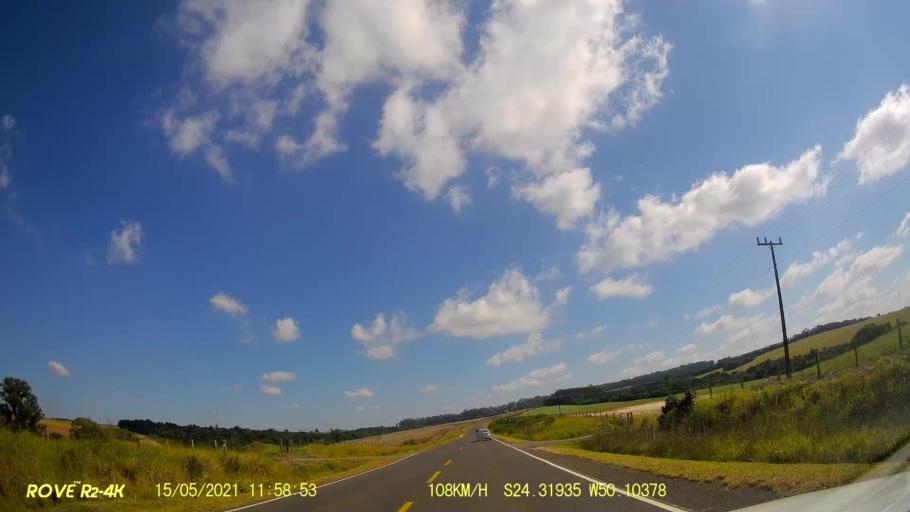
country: BR
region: Parana
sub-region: Pirai Do Sul
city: Pirai do Sul
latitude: -24.3193
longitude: -50.1035
